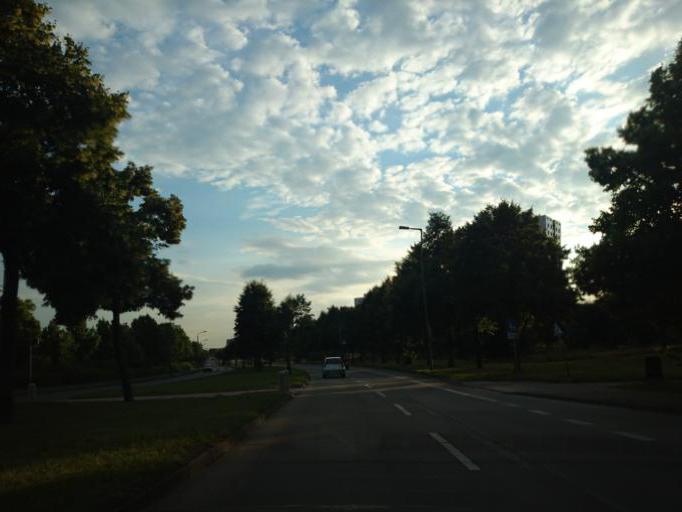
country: DE
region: Berlin
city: Marzahn
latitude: 52.5450
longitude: 13.5574
